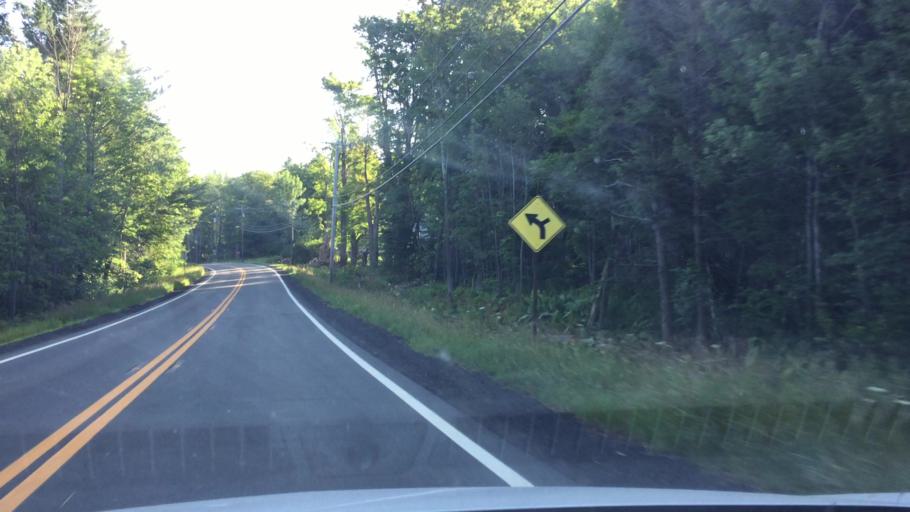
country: US
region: Massachusetts
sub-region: Berkshire County
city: Becket
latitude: 42.2910
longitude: -73.0586
